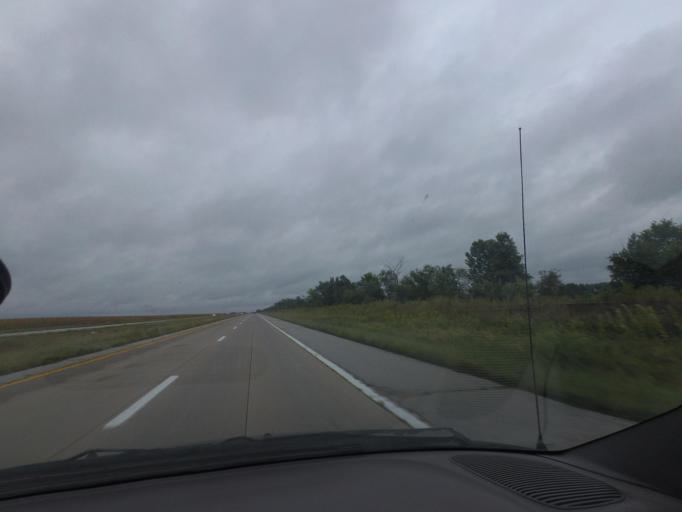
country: US
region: Missouri
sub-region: Marion County
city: Monroe City
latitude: 39.6631
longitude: -91.8380
